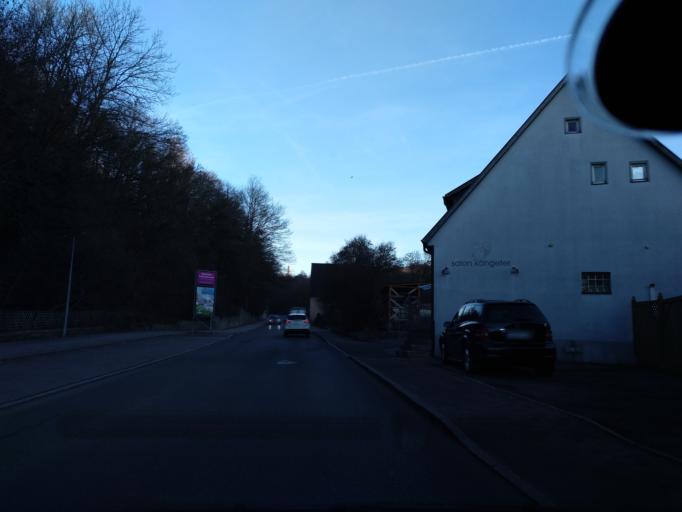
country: DE
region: Baden-Wuerttemberg
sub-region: Regierungsbezirk Stuttgart
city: Schwaebisch Hall
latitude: 49.0991
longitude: 9.7491
